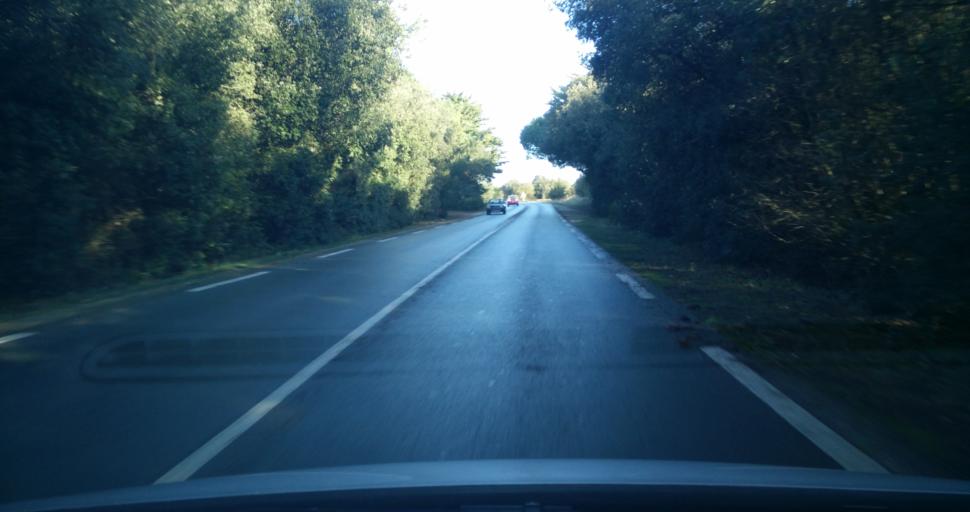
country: FR
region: Poitou-Charentes
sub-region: Departement de la Charente-Maritime
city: La Flotte
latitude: 46.1911
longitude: -1.3463
